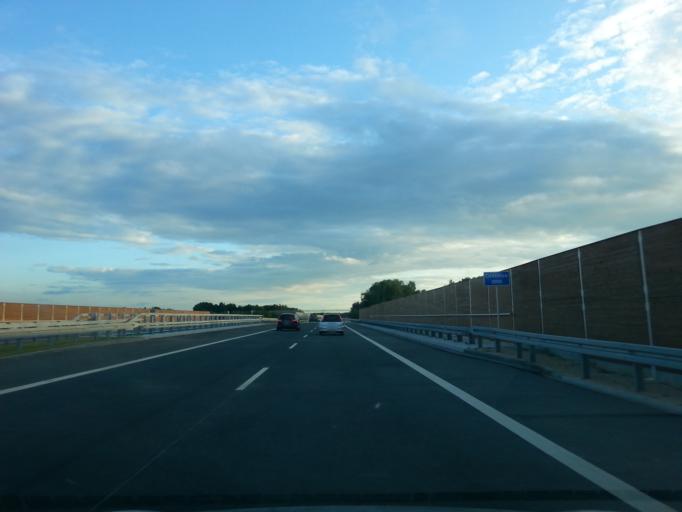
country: PL
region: Lodz Voivodeship
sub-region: Powiat wieruszowski
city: Lututow
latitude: 51.3499
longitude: 18.5124
